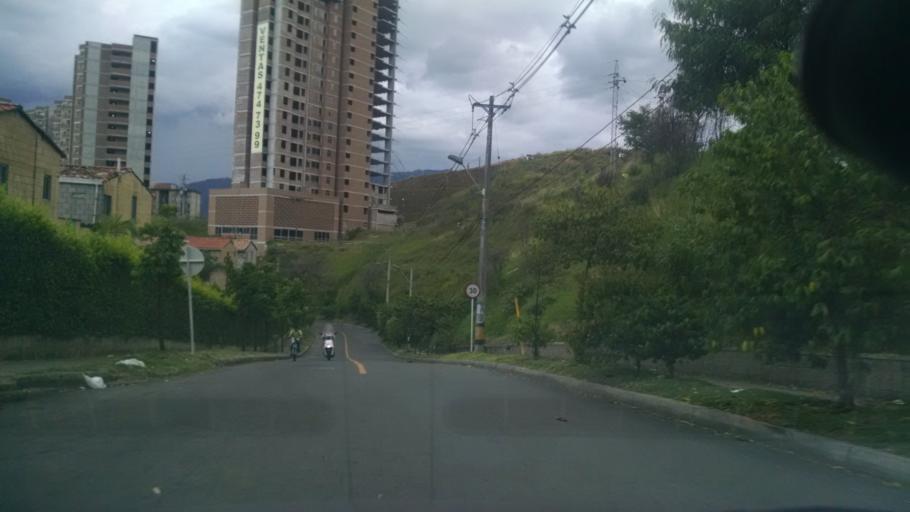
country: CO
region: Antioquia
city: Medellin
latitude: 6.2725
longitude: -75.6023
